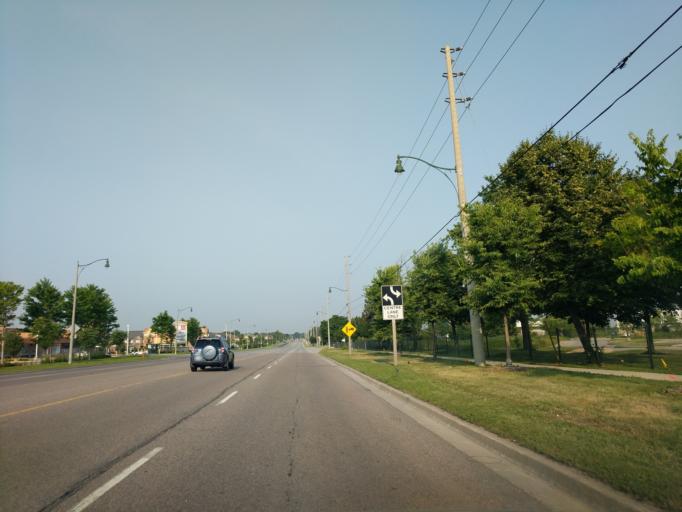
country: CA
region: Ontario
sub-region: York
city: Richmond Hill
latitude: 43.8972
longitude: -79.4018
